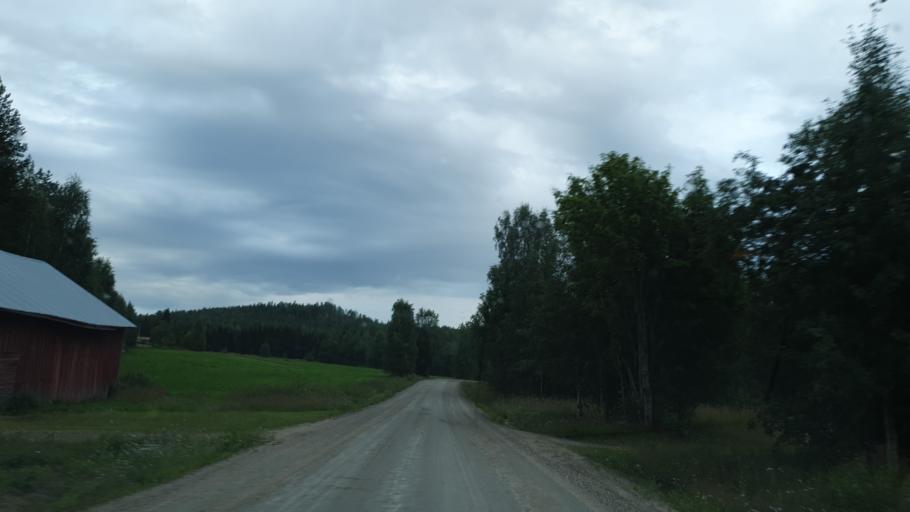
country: FI
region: Kainuu
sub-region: Kehys-Kainuu
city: Kuhmo
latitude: 64.2056
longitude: 29.3722
